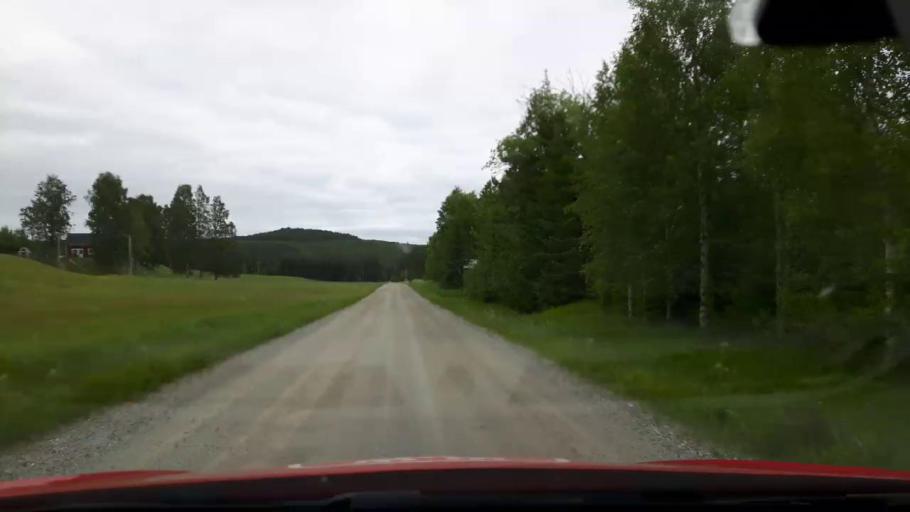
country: SE
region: Jaemtland
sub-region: Ragunda Kommun
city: Hammarstrand
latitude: 63.2118
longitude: 16.0901
